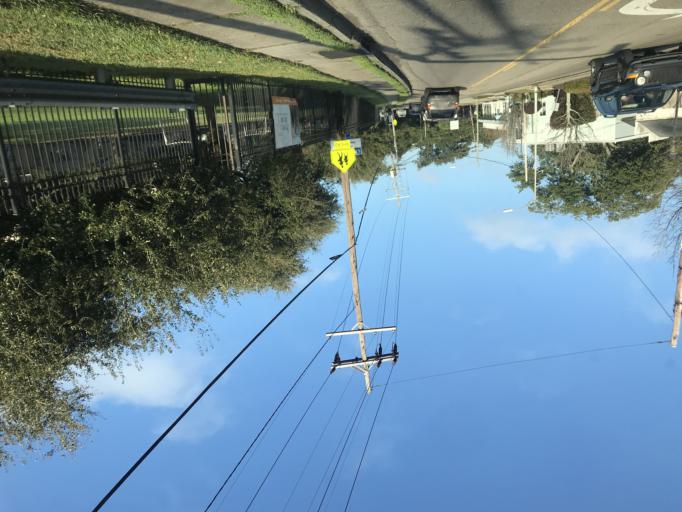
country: US
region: Louisiana
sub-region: Jefferson Parish
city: Metairie
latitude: 29.9804
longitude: -90.1266
